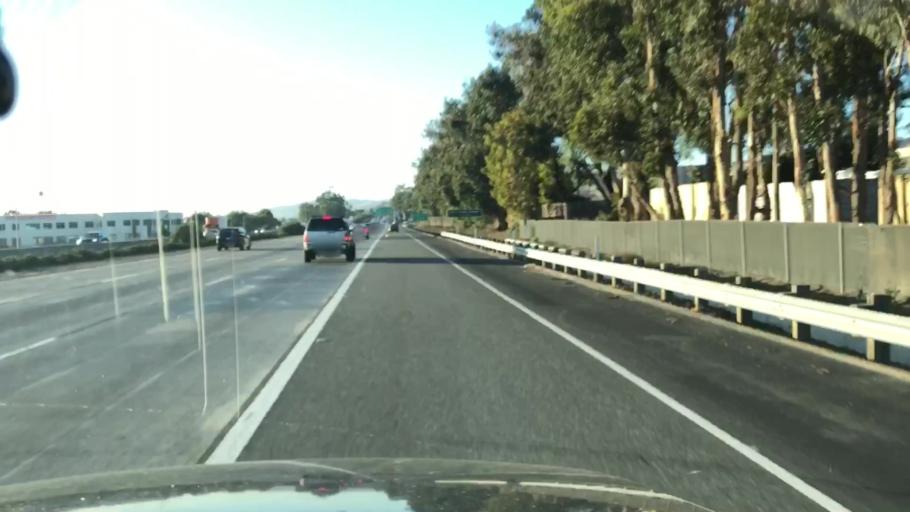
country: US
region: California
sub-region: Ventura County
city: El Rio
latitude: 34.2594
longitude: -119.2244
